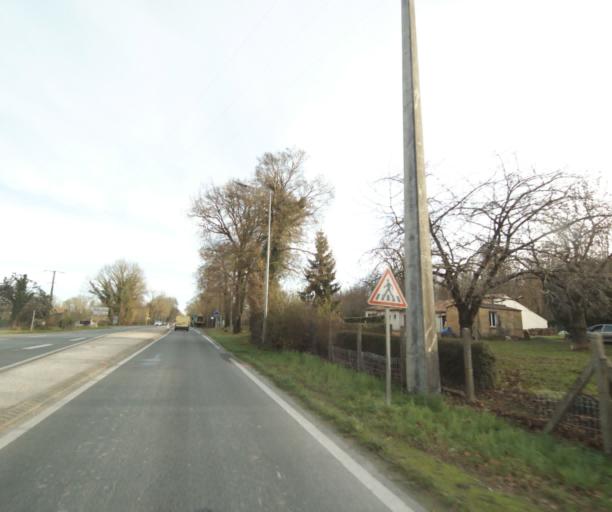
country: FR
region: Poitou-Charentes
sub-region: Departement de la Charente-Maritime
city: Saint-Georges-des-Coteaux
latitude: 45.7779
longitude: -0.7011
